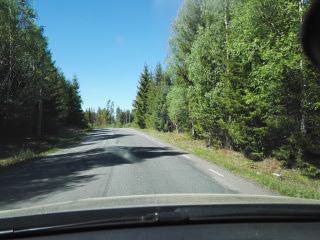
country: SE
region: Kronoberg
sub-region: Vaxjo Kommun
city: Rottne
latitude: 57.0769
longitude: 14.8207
